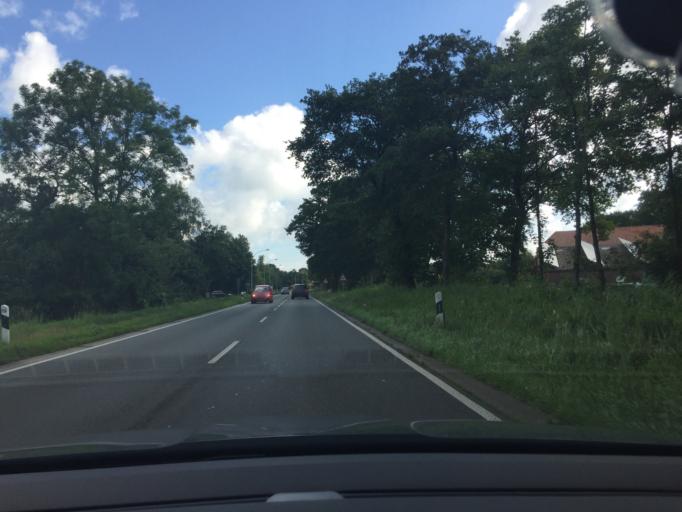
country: DE
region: Lower Saxony
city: Blomberg
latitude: 53.5433
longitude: 7.6051
